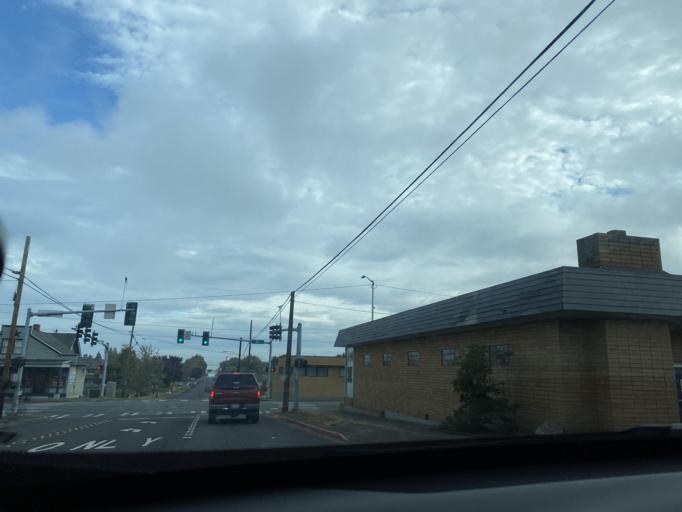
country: US
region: Washington
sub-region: Clallam County
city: Port Angeles
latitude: 48.1103
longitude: -123.4339
